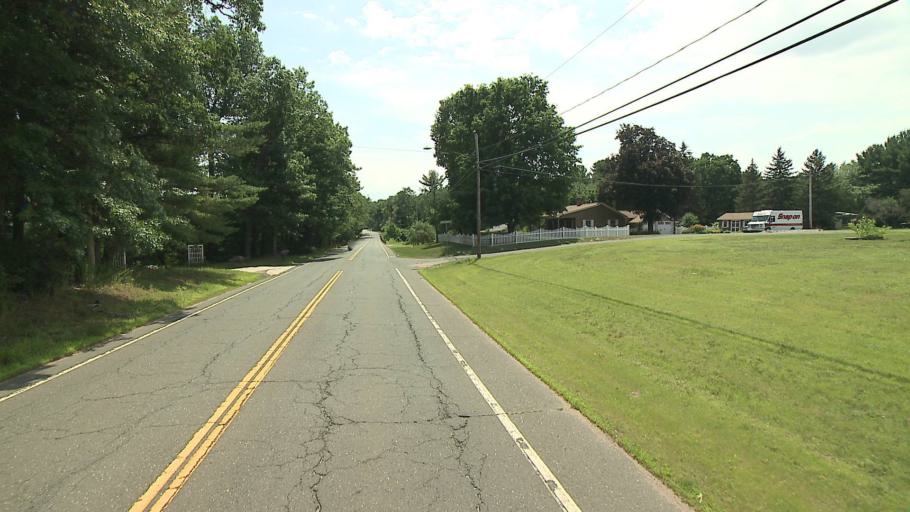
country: US
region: Massachusetts
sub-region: Hampden County
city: Southwick
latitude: 42.0246
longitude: -72.7487
